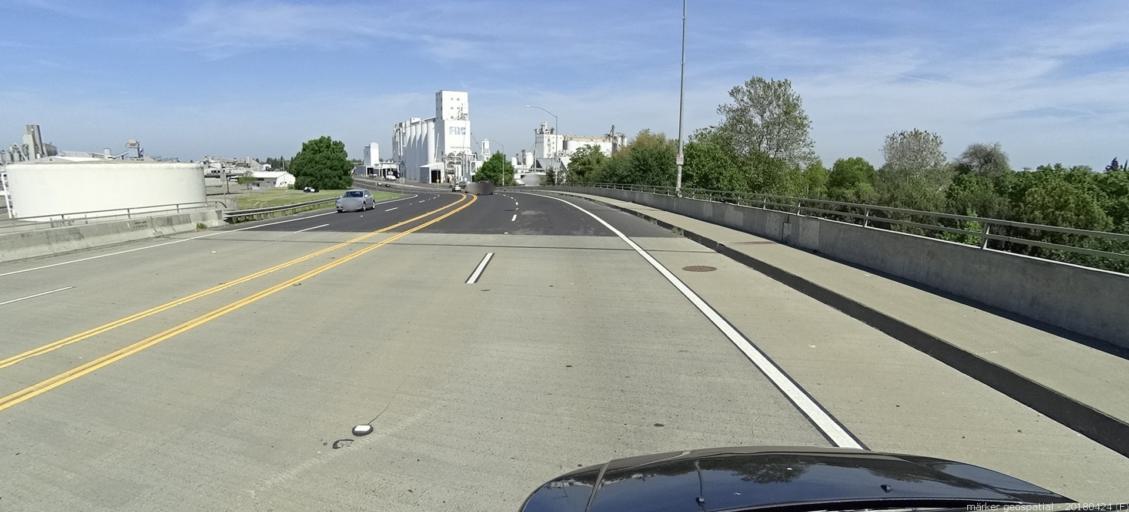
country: US
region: California
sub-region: Yolo County
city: West Sacramento
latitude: 38.5619
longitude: -121.5390
